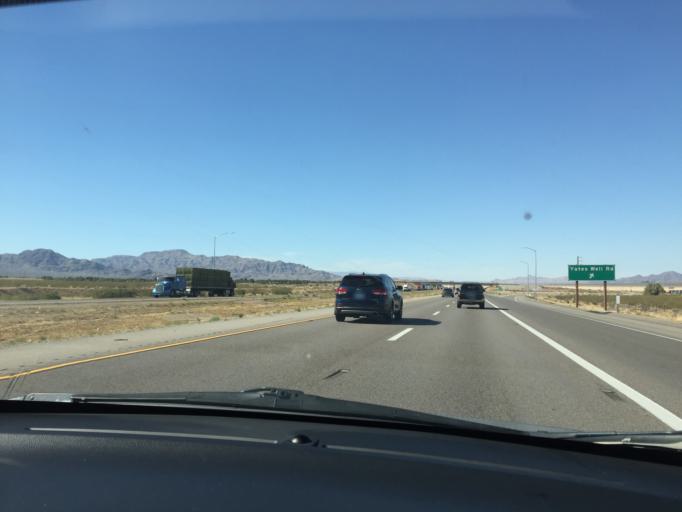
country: US
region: Nevada
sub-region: Clark County
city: Sandy Valley
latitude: 35.5355
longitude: -115.4218
